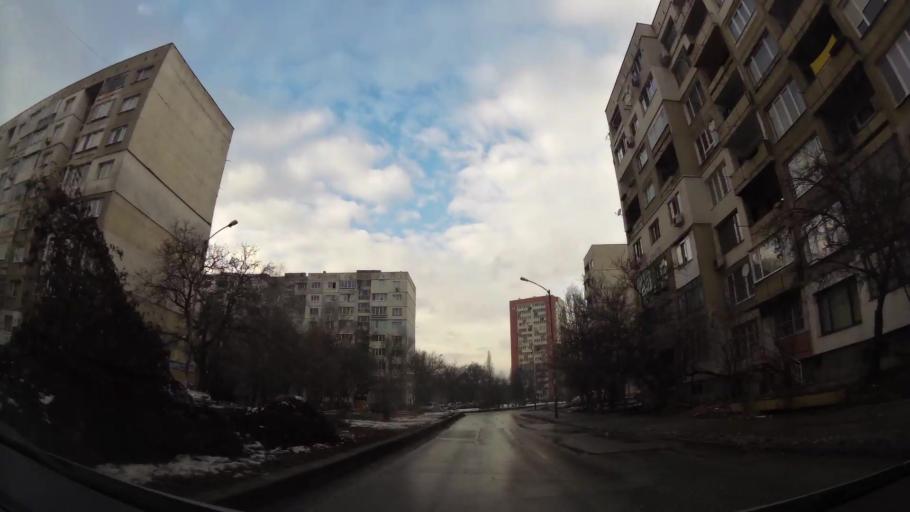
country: BG
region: Sofia-Capital
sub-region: Stolichna Obshtina
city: Sofia
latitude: 42.7085
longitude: 23.2858
